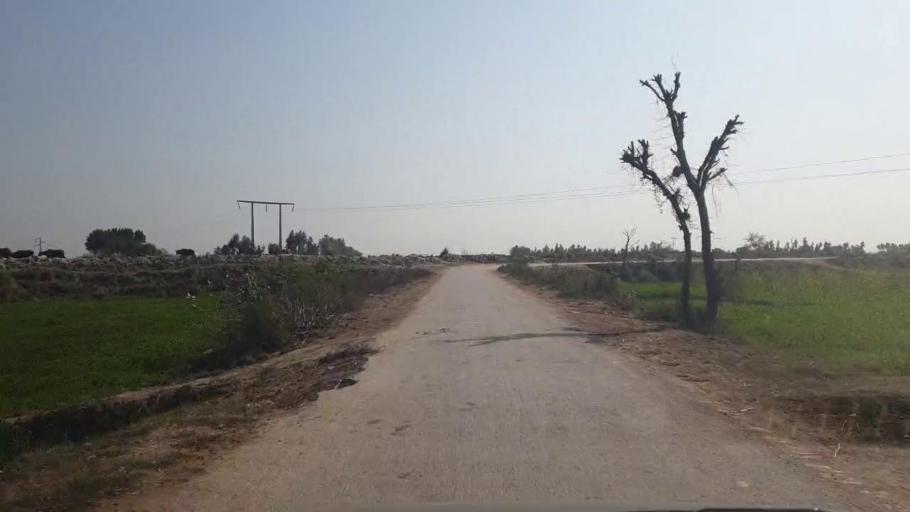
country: PK
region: Sindh
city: Tando Adam
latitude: 25.7427
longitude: 68.6187
